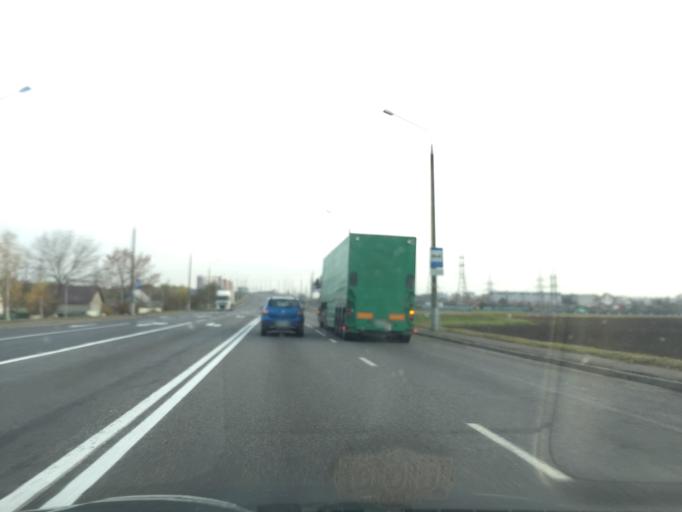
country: BY
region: Gomel
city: Gomel
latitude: 52.4851
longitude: 30.9685
